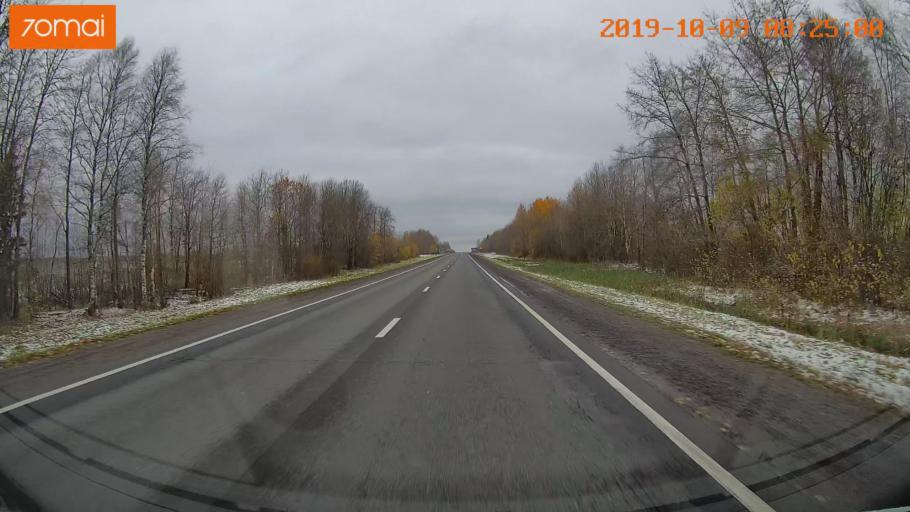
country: RU
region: Vologda
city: Gryazovets
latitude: 58.7744
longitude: 40.2750
